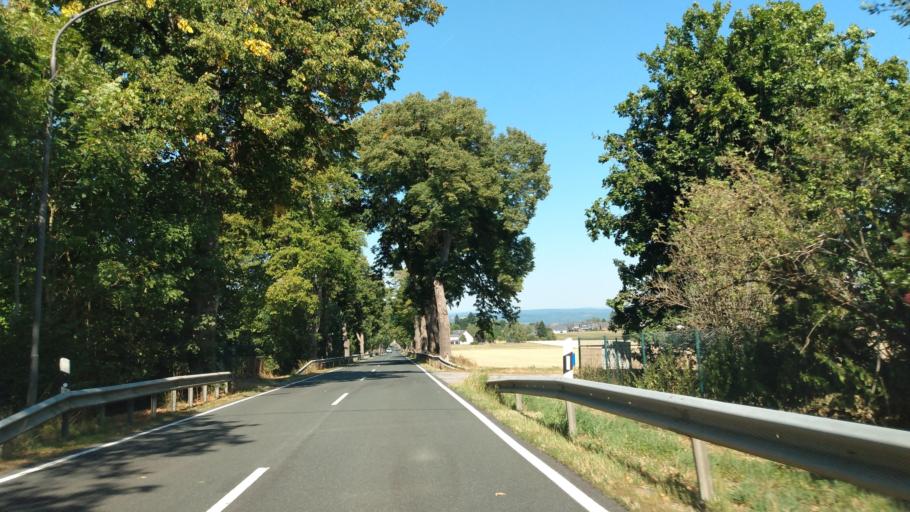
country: DE
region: Rheinland-Pfalz
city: Irmenach
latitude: 49.9182
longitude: 7.1973
